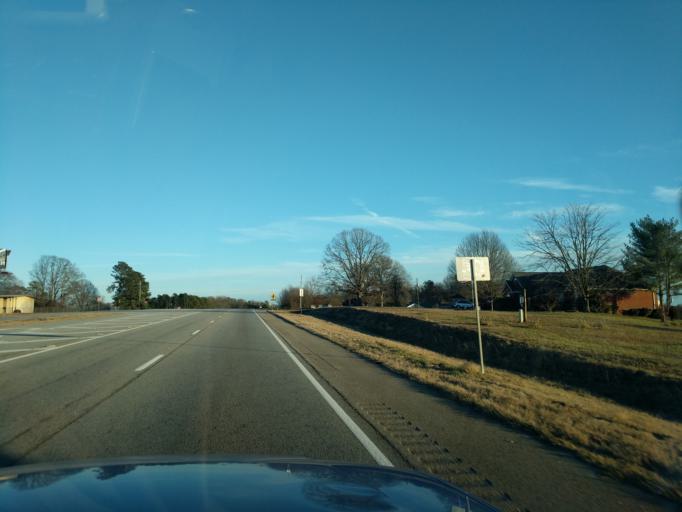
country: US
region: Georgia
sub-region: Franklin County
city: Lavonia
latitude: 34.4545
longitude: -83.1550
